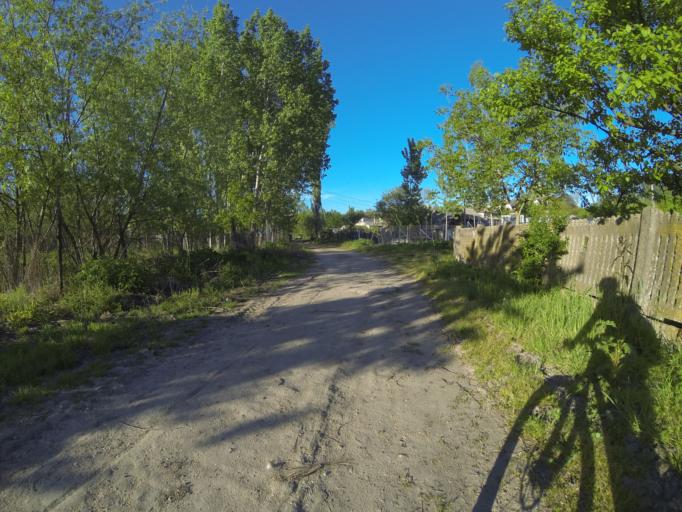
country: RO
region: Dolj
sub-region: Comuna Segarcea
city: Segarcea
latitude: 44.0951
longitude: 23.7403
